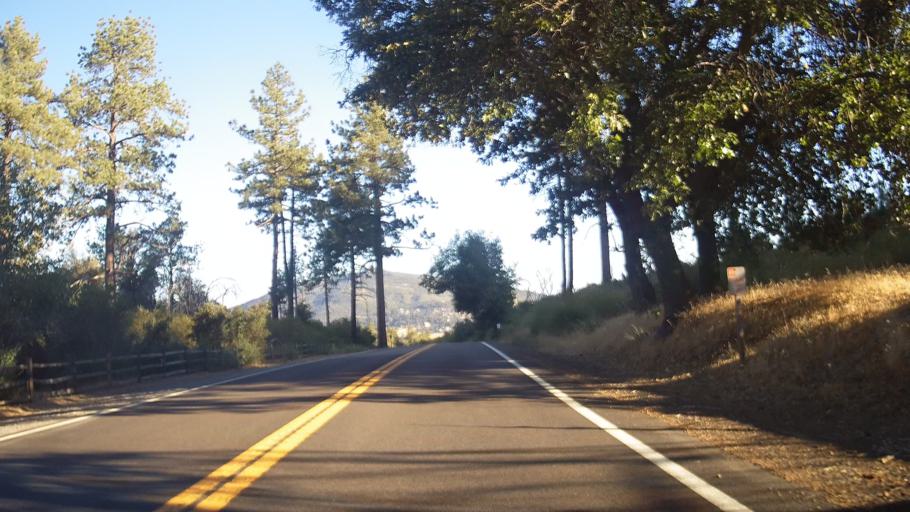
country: US
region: California
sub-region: San Diego County
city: Descanso
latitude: 32.9608
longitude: -116.5792
